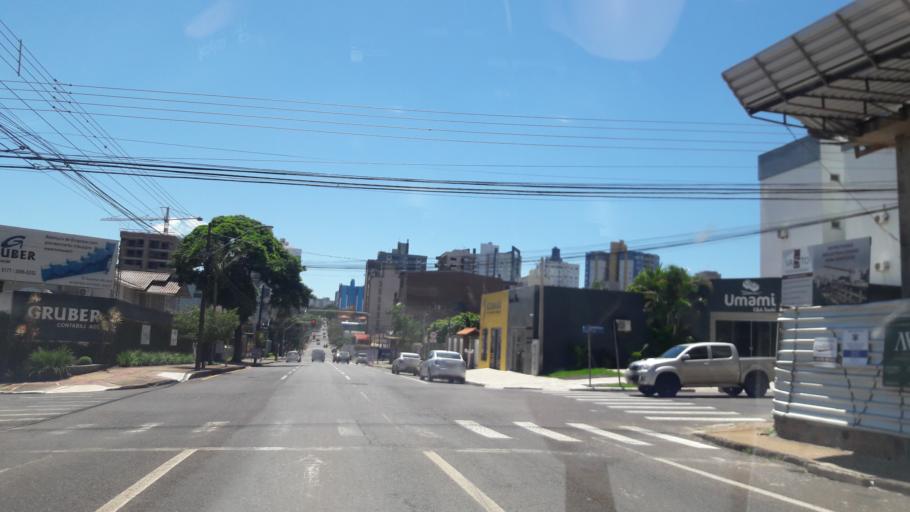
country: BR
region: Parana
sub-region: Cascavel
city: Cascavel
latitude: -24.9514
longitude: -53.4713
